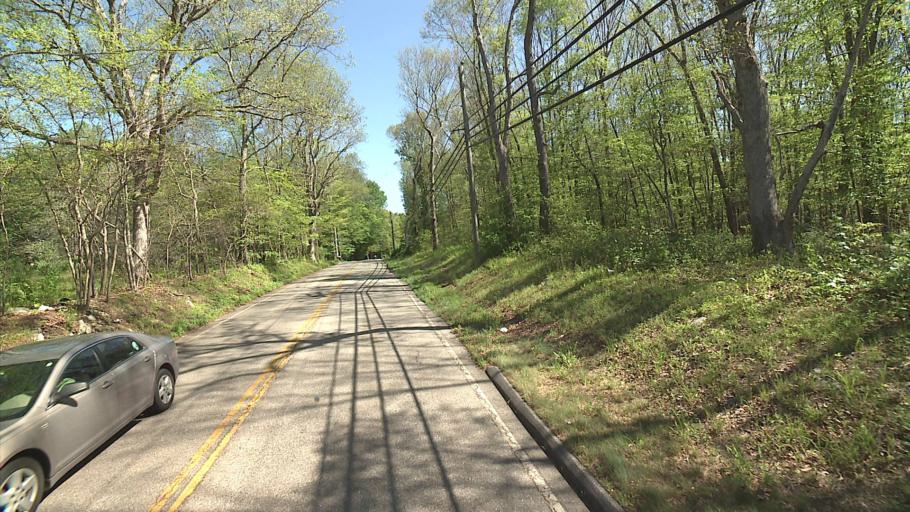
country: US
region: Connecticut
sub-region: New London County
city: Colchester
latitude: 41.5850
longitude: -72.3100
